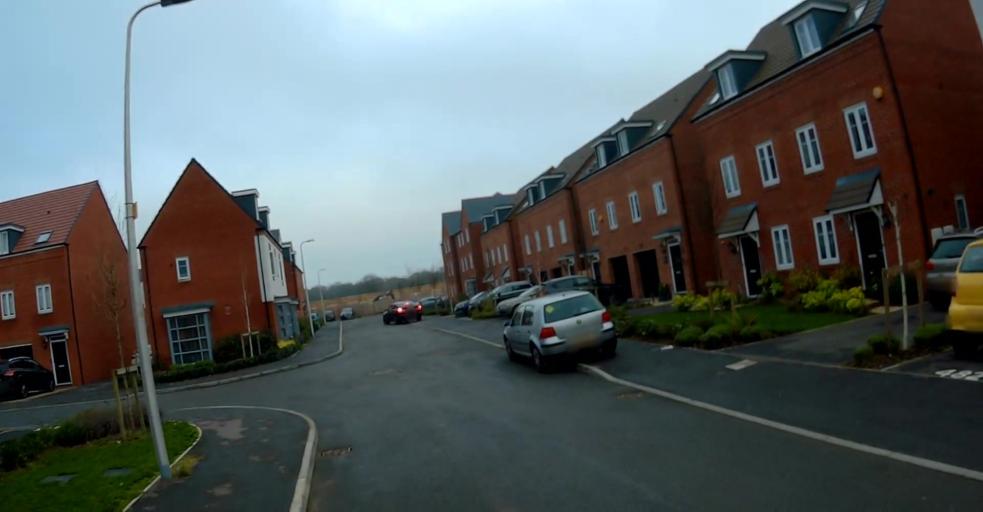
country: GB
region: England
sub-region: Wokingham
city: Wokingham
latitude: 51.4069
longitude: -0.8081
